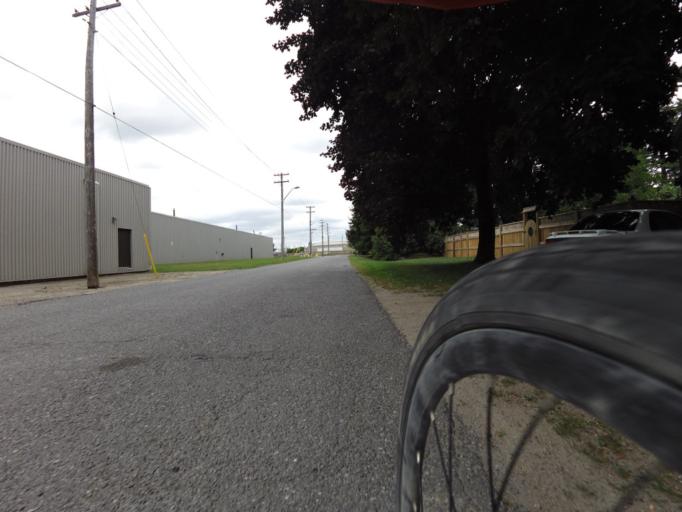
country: CA
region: Ontario
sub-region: Lanark County
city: Smiths Falls
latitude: 44.9028
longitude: -76.0267
